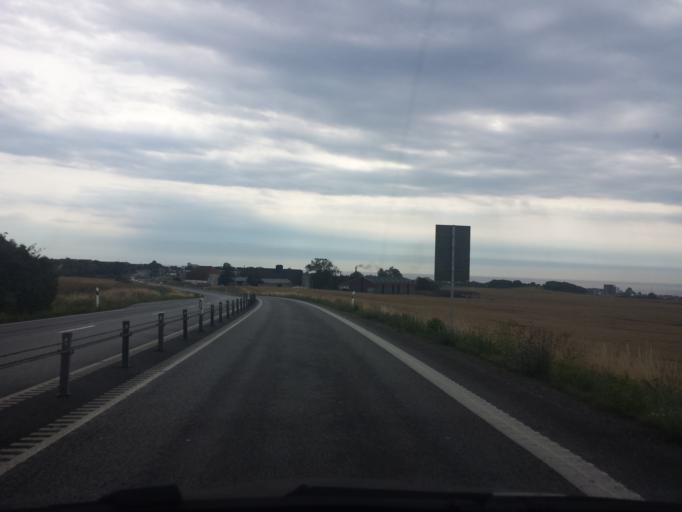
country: SE
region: Skane
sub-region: Ystads Kommun
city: Ystad
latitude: 55.4432
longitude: 13.7806
